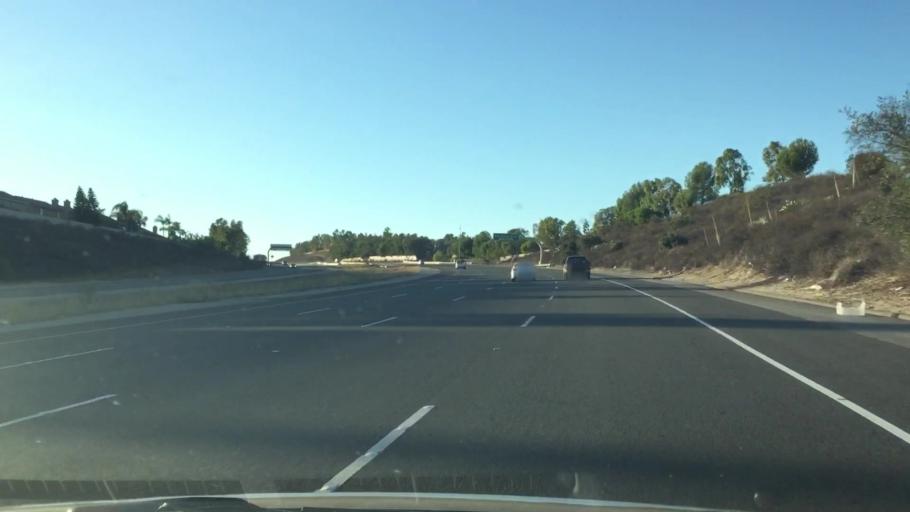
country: US
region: California
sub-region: Orange County
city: Rancho Santa Margarita
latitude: 33.6502
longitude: -117.6084
